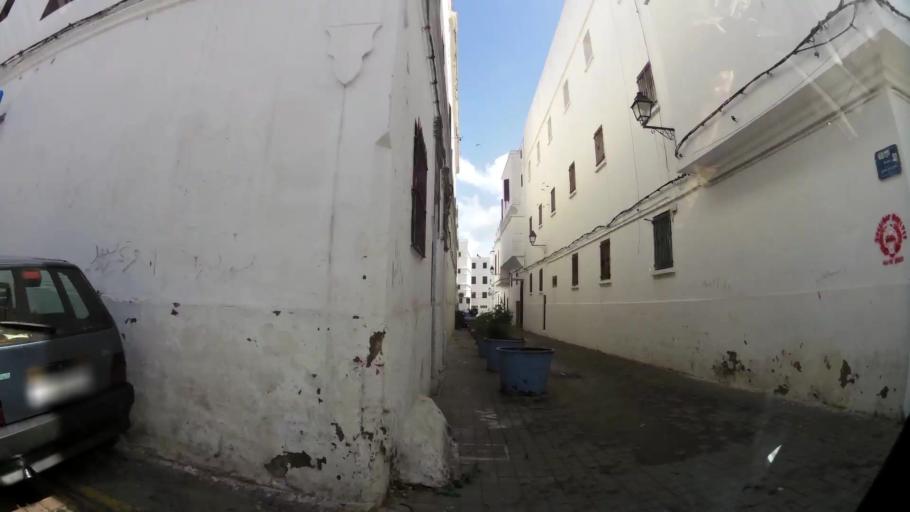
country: MA
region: Grand Casablanca
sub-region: Casablanca
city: Casablanca
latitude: 33.6016
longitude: -7.6199
